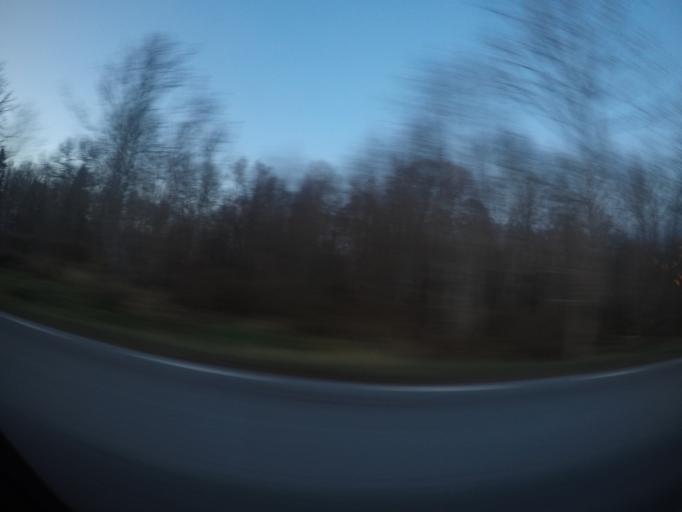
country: SE
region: OErebro
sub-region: Lindesbergs Kommun
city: Fellingsbro
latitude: 59.3261
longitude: 15.4765
